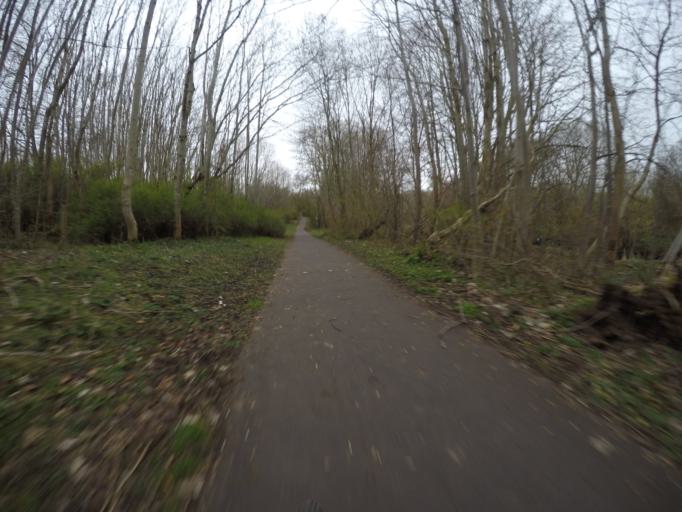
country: GB
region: Scotland
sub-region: North Ayrshire
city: Irvine
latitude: 55.6125
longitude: -4.6415
